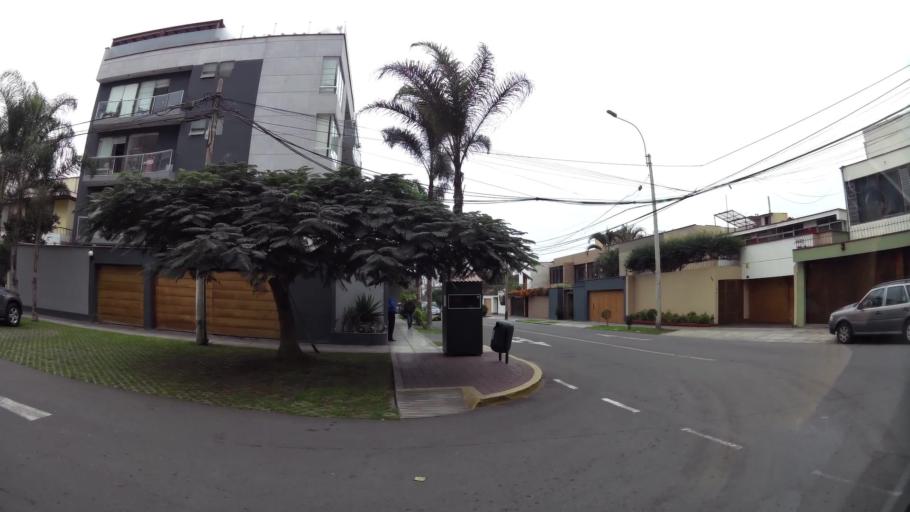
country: PE
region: Lima
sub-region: Lima
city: Surco
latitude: -12.1194
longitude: -77.0173
